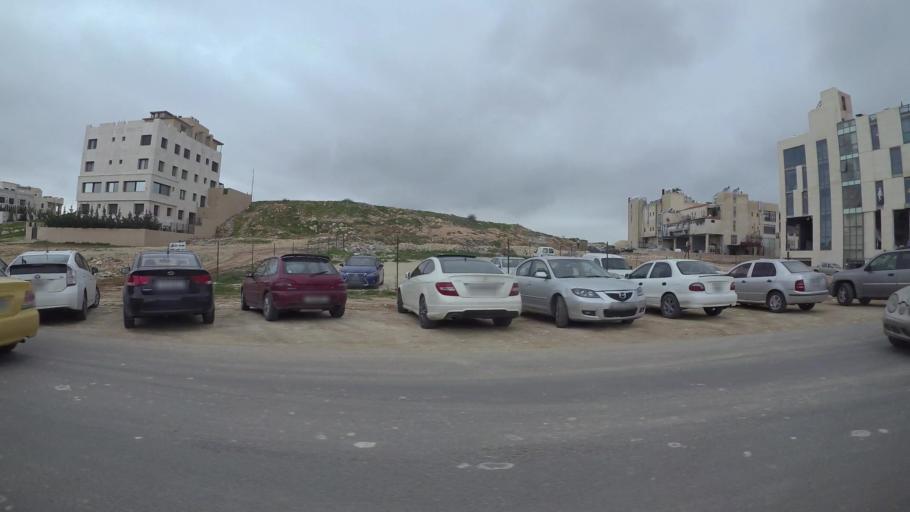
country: JO
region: Amman
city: Al Jubayhah
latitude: 31.9953
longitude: 35.8364
